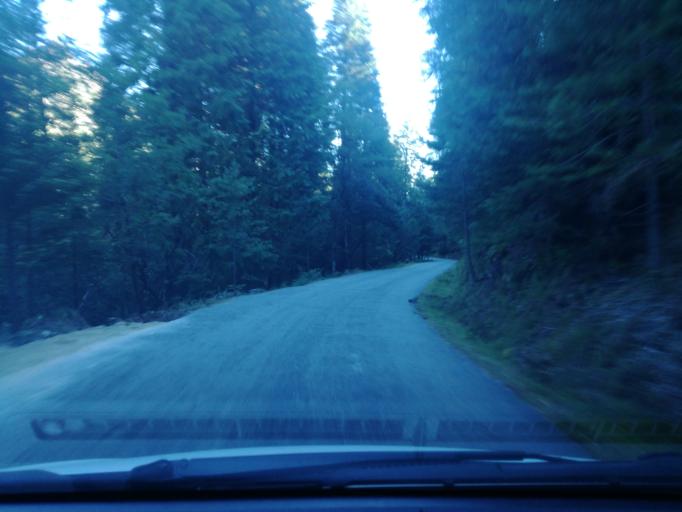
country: ES
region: Galicia
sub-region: Provincia de Ourense
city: Lobios
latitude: 41.7747
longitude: -8.1433
